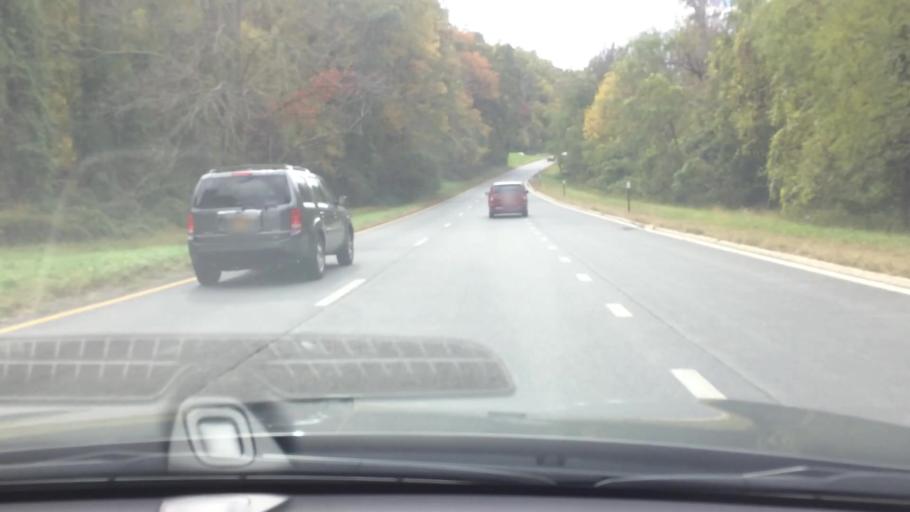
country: US
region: New York
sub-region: Dutchess County
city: Hillside Lake
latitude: 41.5340
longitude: -73.7723
